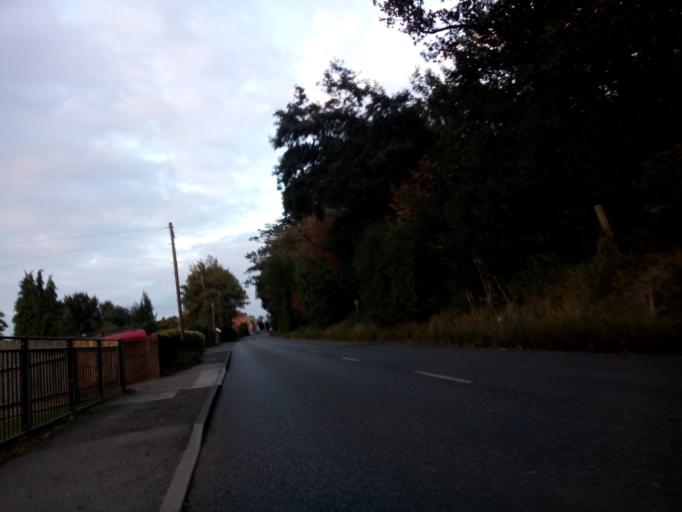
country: GB
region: England
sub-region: Suffolk
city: Bramford
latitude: 52.0549
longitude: 1.1148
